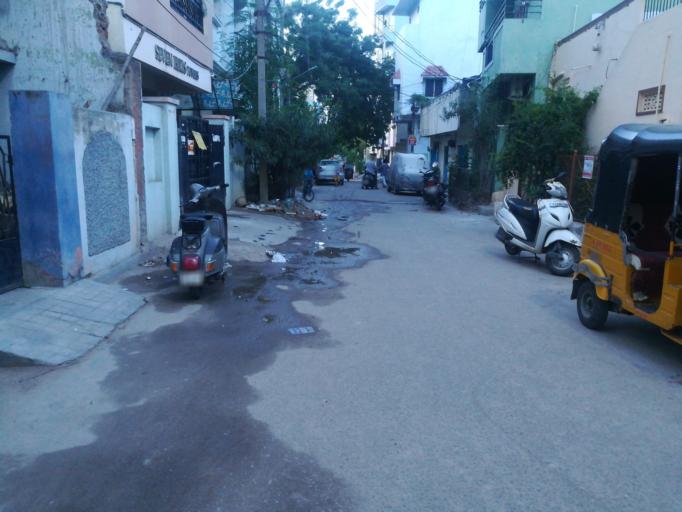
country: IN
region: Telangana
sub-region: Hyderabad
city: Malkajgiri
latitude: 17.4205
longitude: 78.5161
